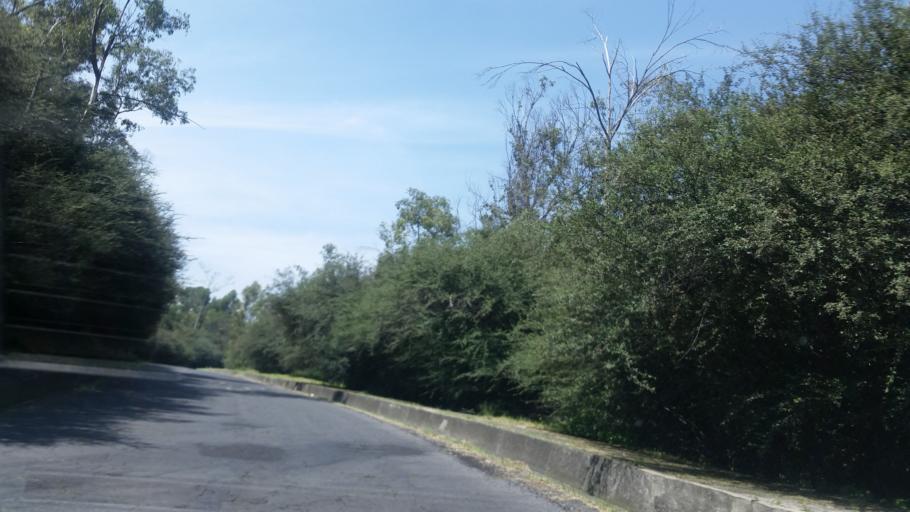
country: MX
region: Mexico City
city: Polanco
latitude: 19.4077
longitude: -99.2131
